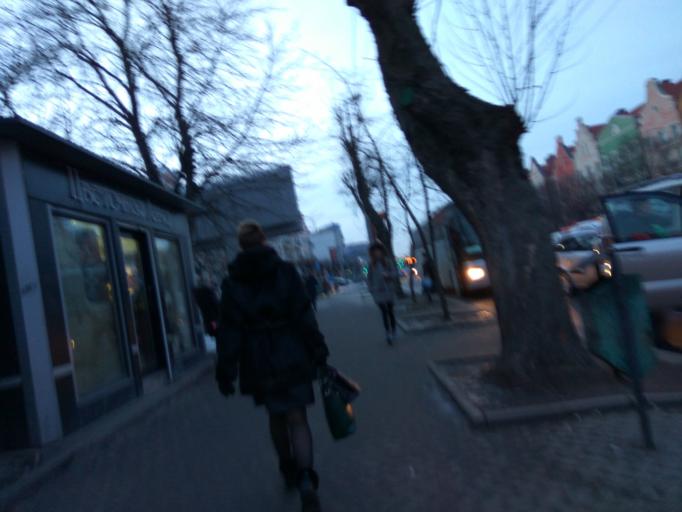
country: RU
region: Kaliningrad
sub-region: Gorod Kaliningrad
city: Kaliningrad
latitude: 54.7128
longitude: 20.5073
